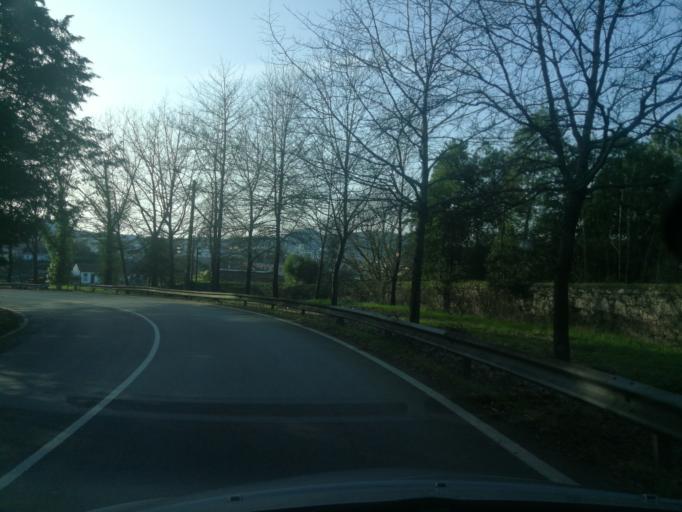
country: PT
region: Braga
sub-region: Barcelos
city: Barcelos
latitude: 41.5254
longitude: -8.6147
